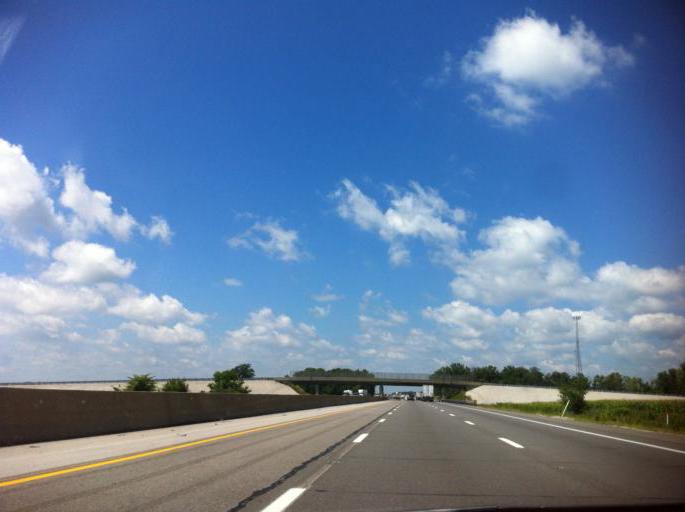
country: US
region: Ohio
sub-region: Sandusky County
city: Clyde
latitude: 41.3834
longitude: -83.0287
